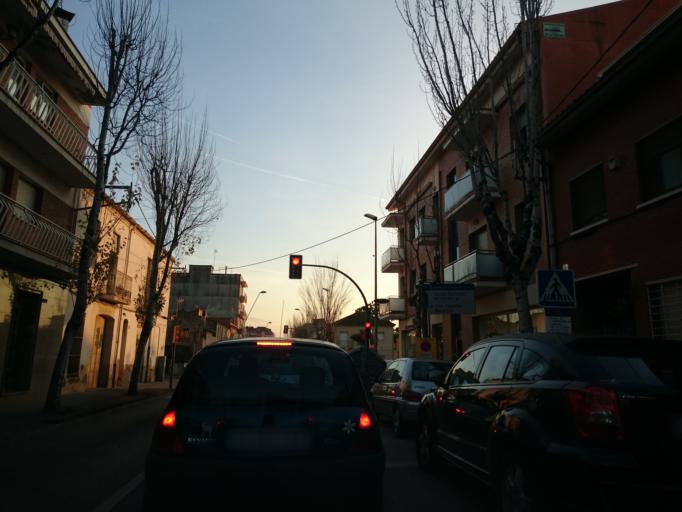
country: ES
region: Catalonia
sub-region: Provincia de Barcelona
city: Les Franqueses del Valles
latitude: 41.6251
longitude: 2.2940
